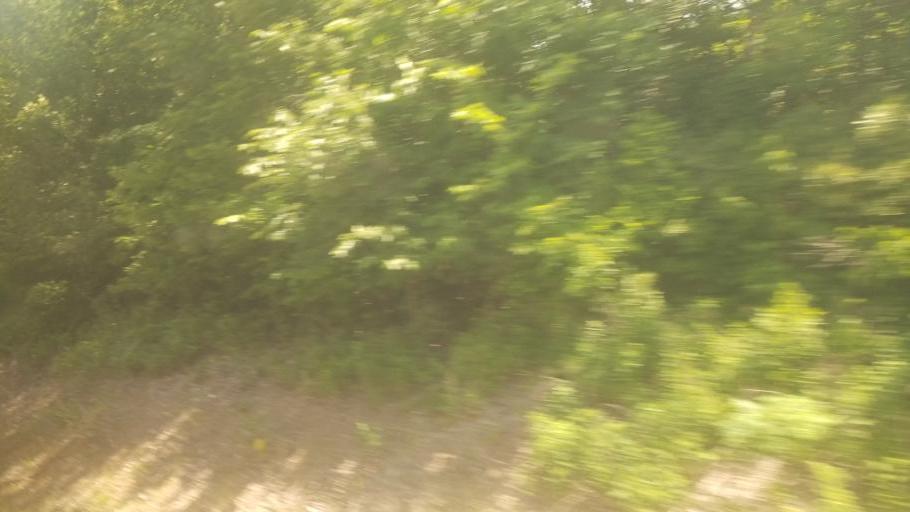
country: US
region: Missouri
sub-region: Linn County
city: Marceline
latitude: 39.8576
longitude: -92.8082
